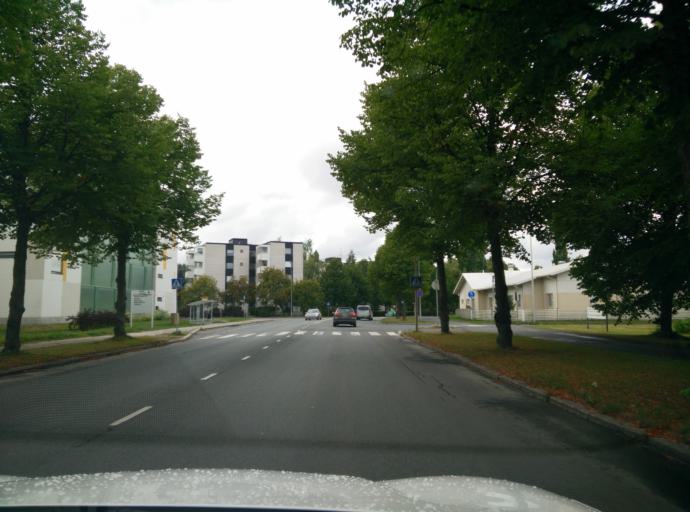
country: FI
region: Haeme
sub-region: Haemeenlinna
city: Haemeenlinna
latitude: 60.9985
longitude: 24.4343
